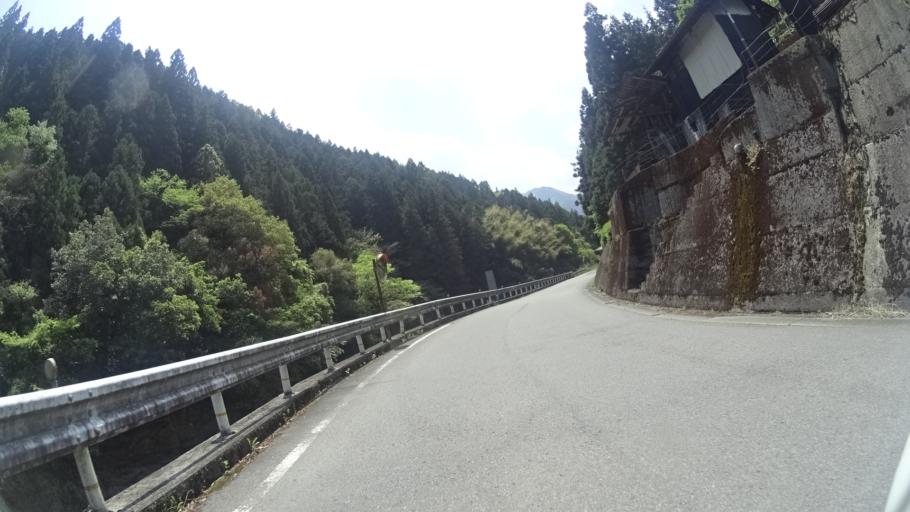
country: JP
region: Tokushima
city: Wakimachi
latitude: 33.9598
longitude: 134.0800
